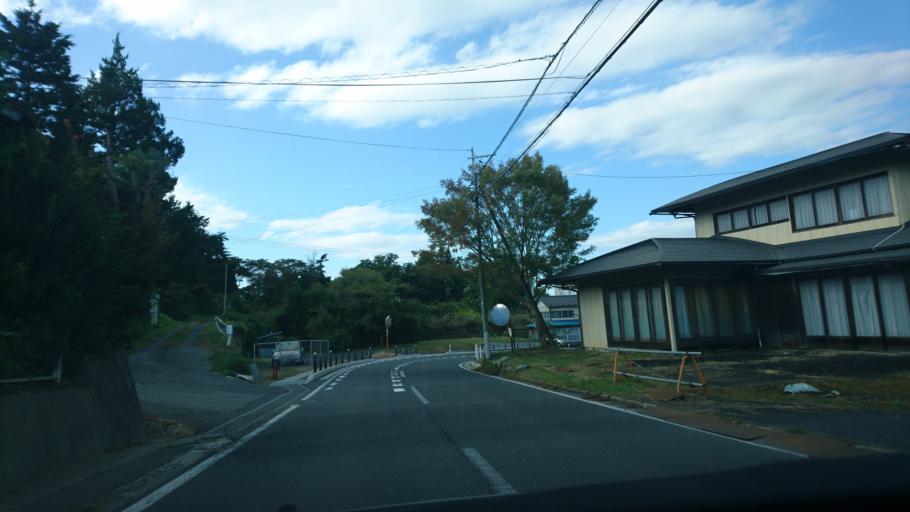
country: JP
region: Iwate
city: Ichinoseki
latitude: 38.8644
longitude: 141.3489
